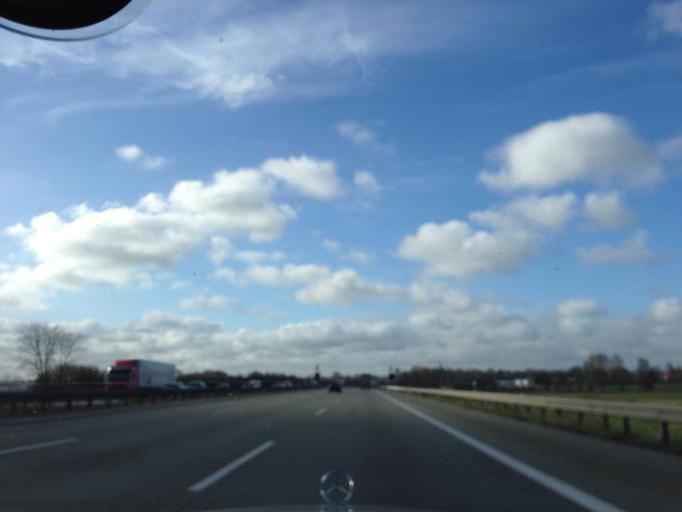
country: DE
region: Hamburg
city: Harburg
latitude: 53.4319
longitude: 10.0334
